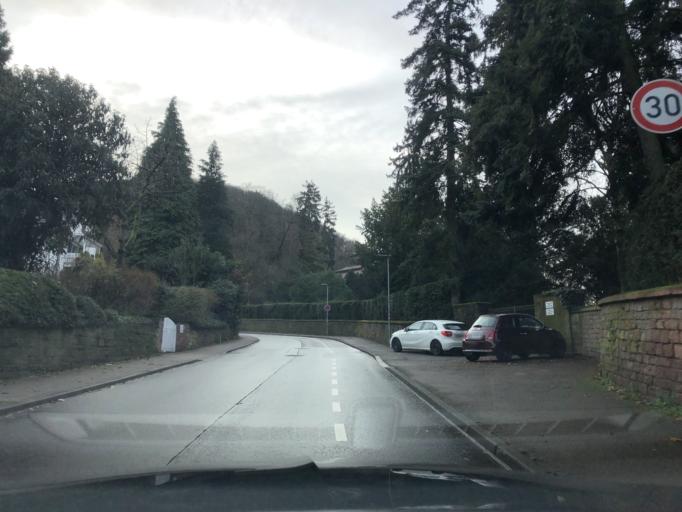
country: DE
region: Baden-Wuerttemberg
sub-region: Karlsruhe Region
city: Heidelberg
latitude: 49.3984
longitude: 8.6929
